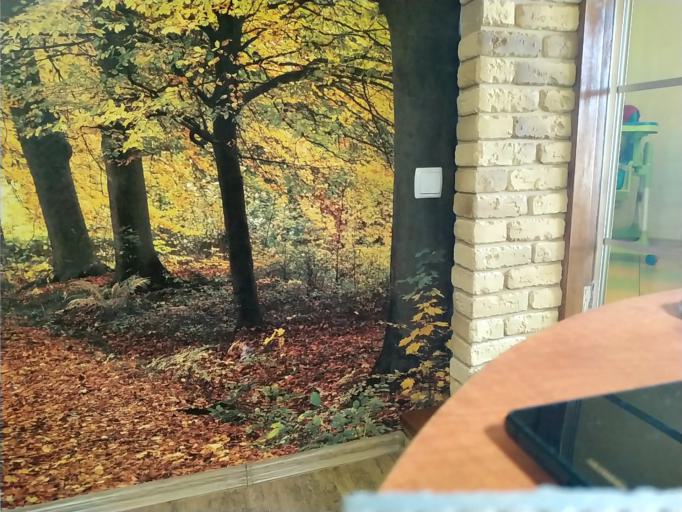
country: RU
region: Kaluga
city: Kondrovo
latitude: 54.8157
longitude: 35.9493
